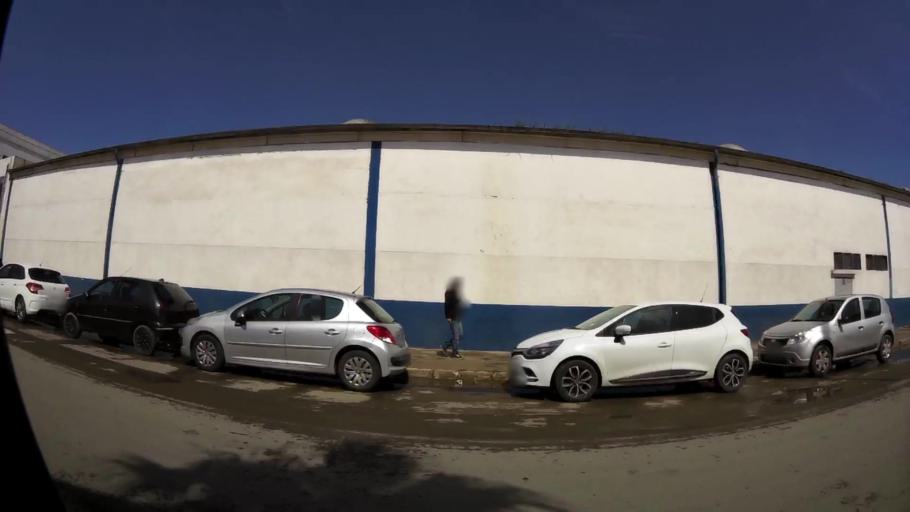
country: MA
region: Grand Casablanca
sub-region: Mediouna
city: Tit Mellil
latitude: 33.6251
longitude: -7.5053
